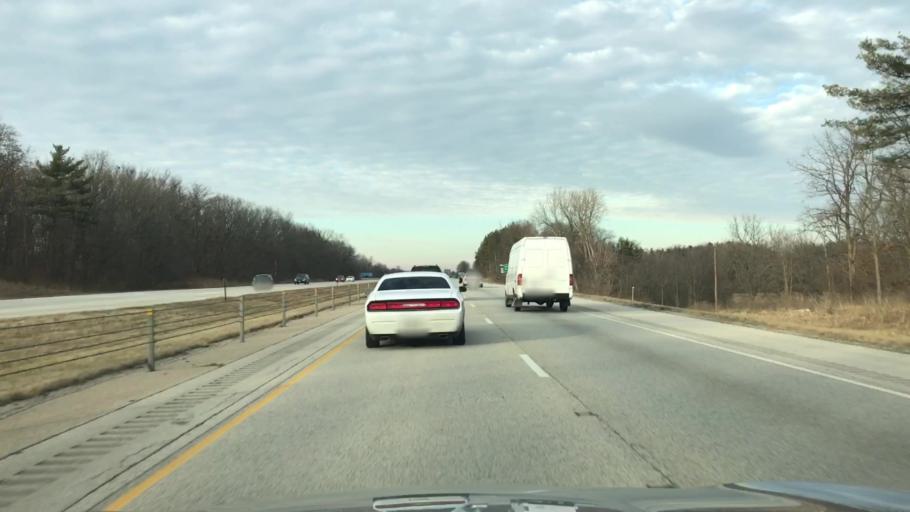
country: US
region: Illinois
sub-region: Sangamon County
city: Sherman
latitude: 39.8808
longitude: -89.5965
